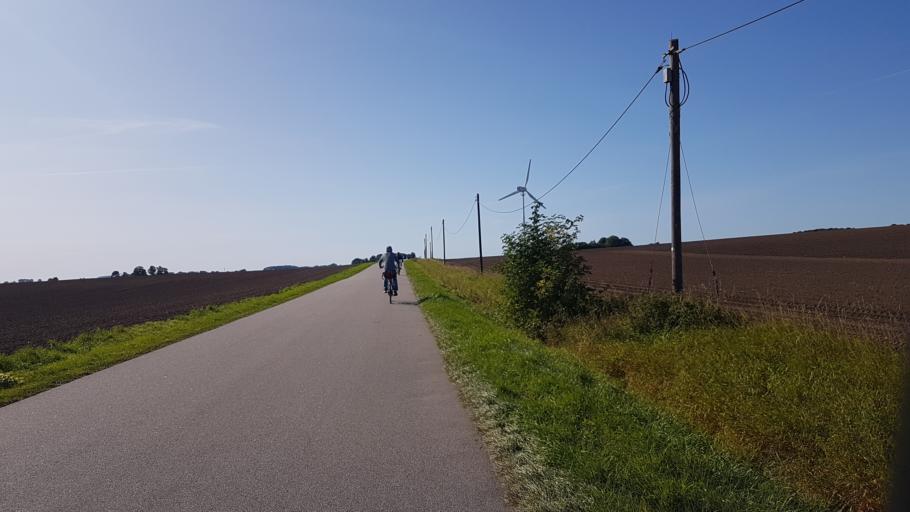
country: DE
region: Mecklenburg-Vorpommern
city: Altenkirchen
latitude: 54.6596
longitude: 13.3336
